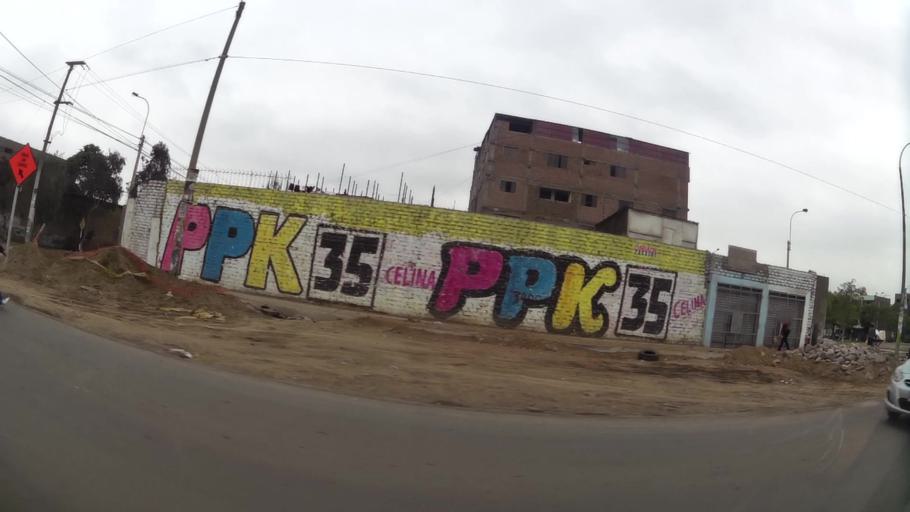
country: PE
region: Lima
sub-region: Lima
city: Vitarte
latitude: -12.0475
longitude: -76.9578
